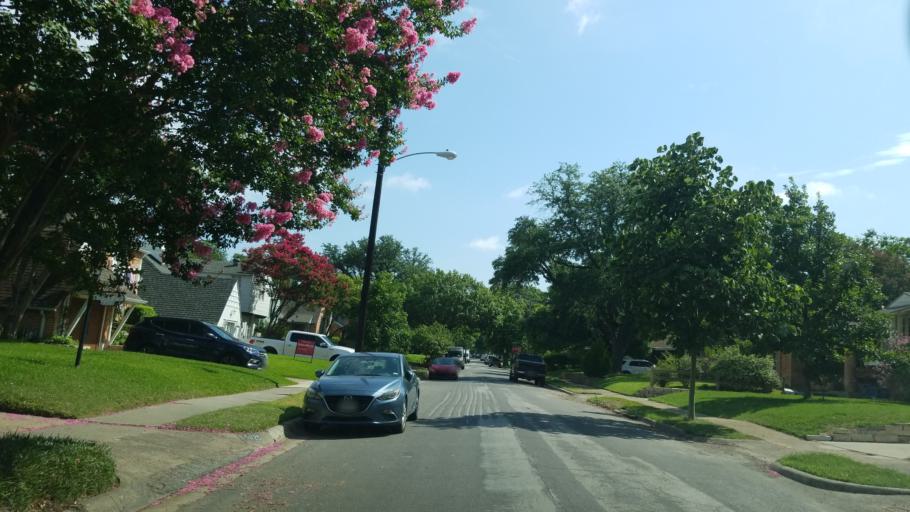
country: US
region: Texas
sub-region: Dallas County
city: Highland Park
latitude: 32.8172
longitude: -96.7863
